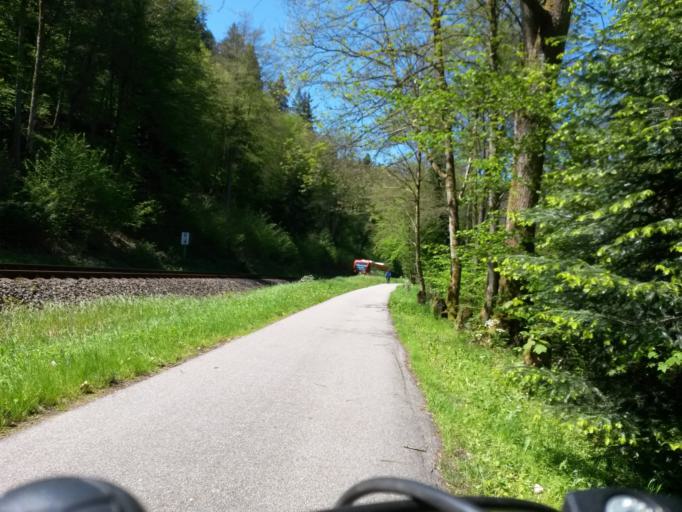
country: DE
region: Baden-Wuerttemberg
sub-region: Karlsruhe Region
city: Engelsbrand
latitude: 48.8374
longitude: 8.6813
